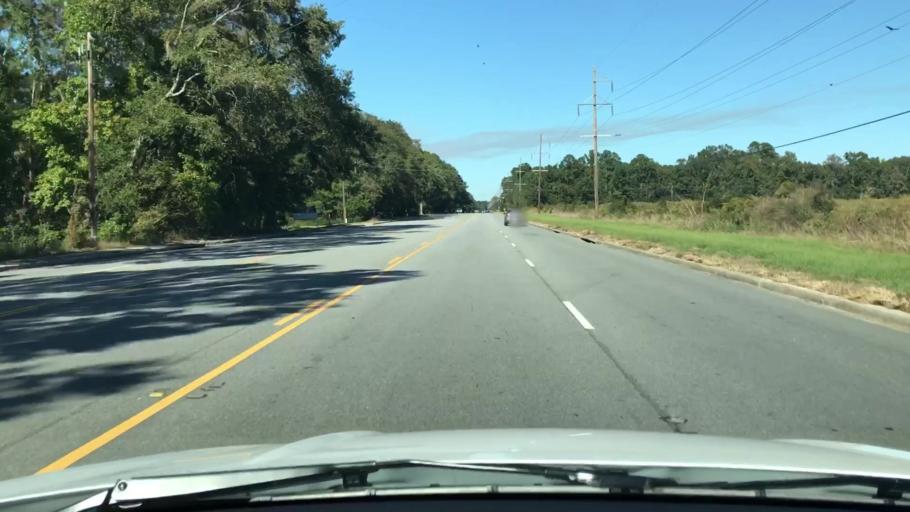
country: US
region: South Carolina
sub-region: Beaufort County
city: Laurel Bay
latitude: 32.5641
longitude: -80.7436
